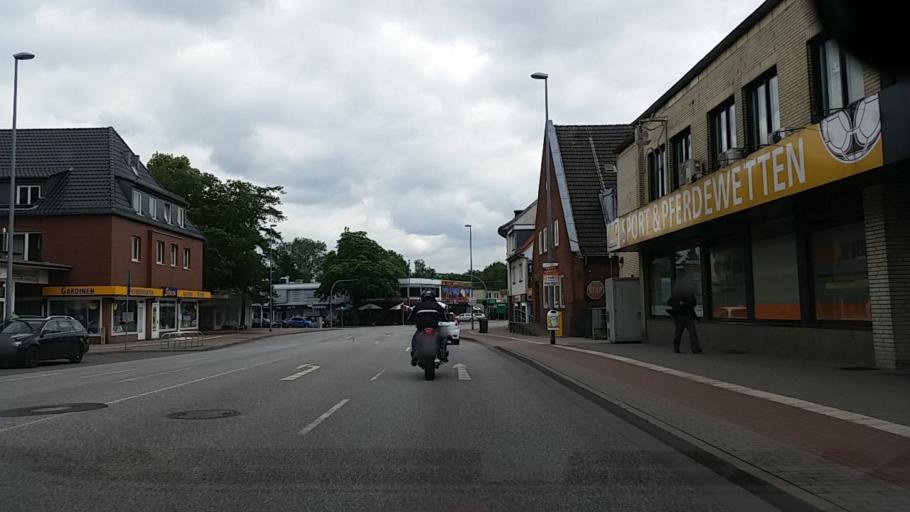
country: DE
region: Hamburg
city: Langenhorn
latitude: 53.6820
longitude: 9.9971
